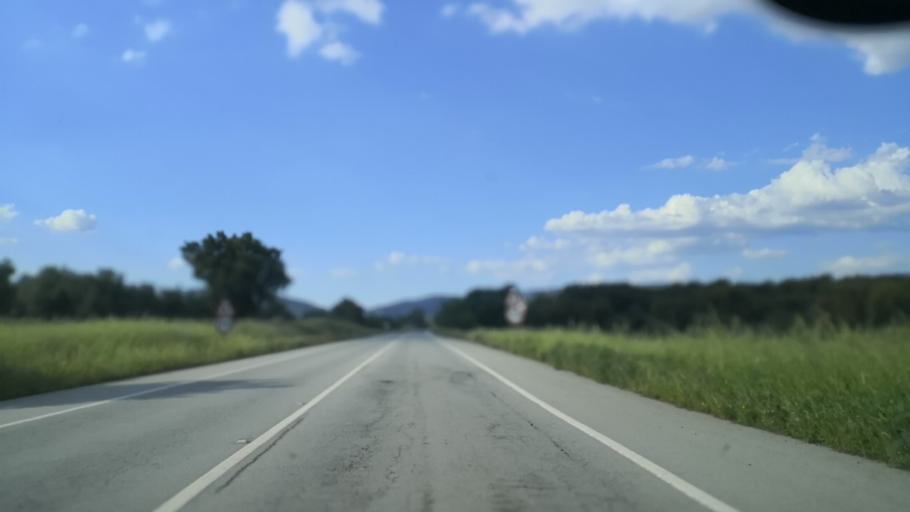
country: PT
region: Portalegre
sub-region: Portalegre
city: Portalegre
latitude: 39.2526
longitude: -7.4478
